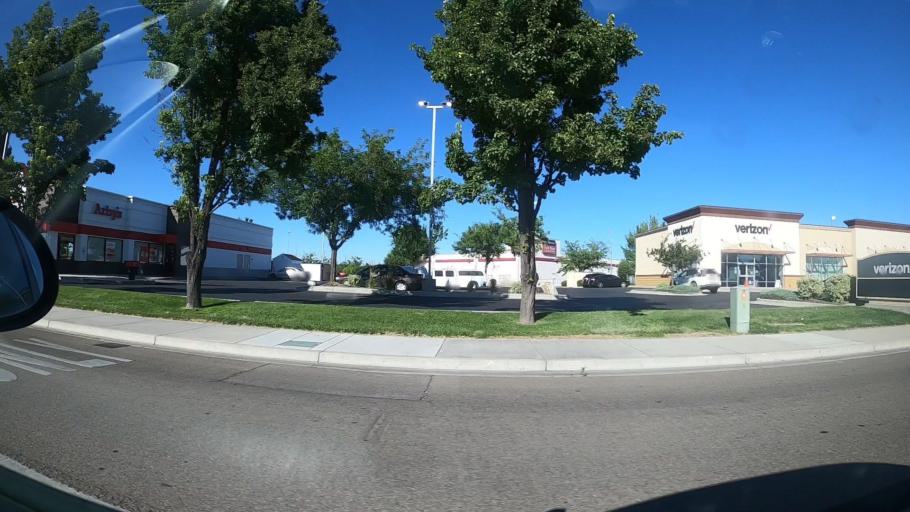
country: US
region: Idaho
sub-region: Canyon County
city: Nampa
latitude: 43.6001
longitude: -116.5952
